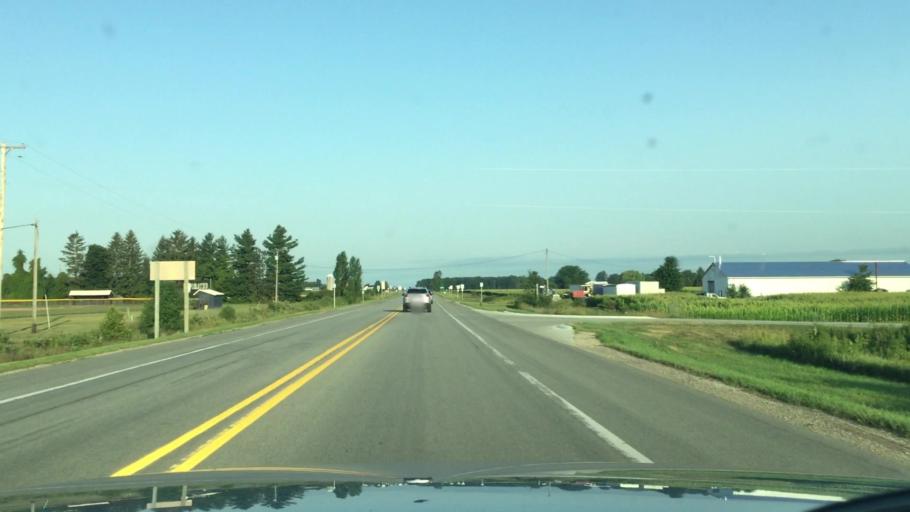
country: US
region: Michigan
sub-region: Montcalm County
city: Carson City
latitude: 43.1763
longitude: -84.7110
